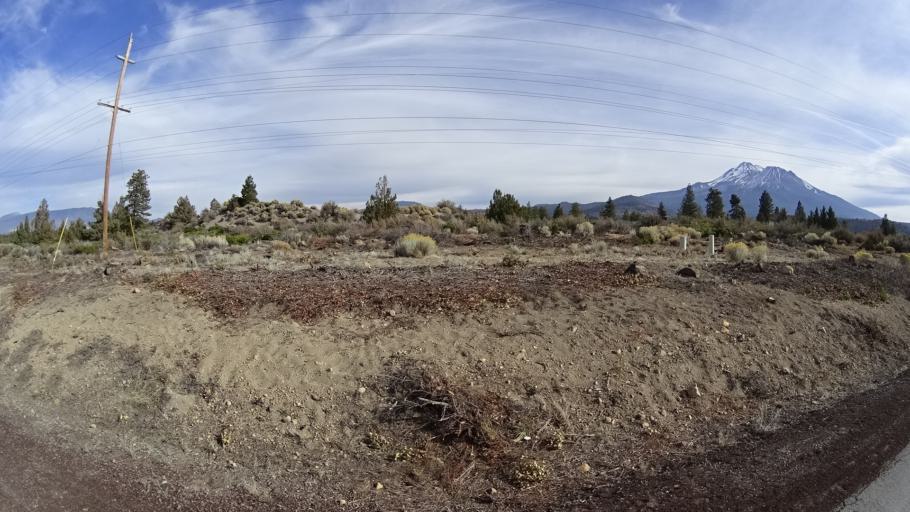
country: US
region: California
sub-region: Siskiyou County
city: Weed
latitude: 41.4954
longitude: -122.3626
